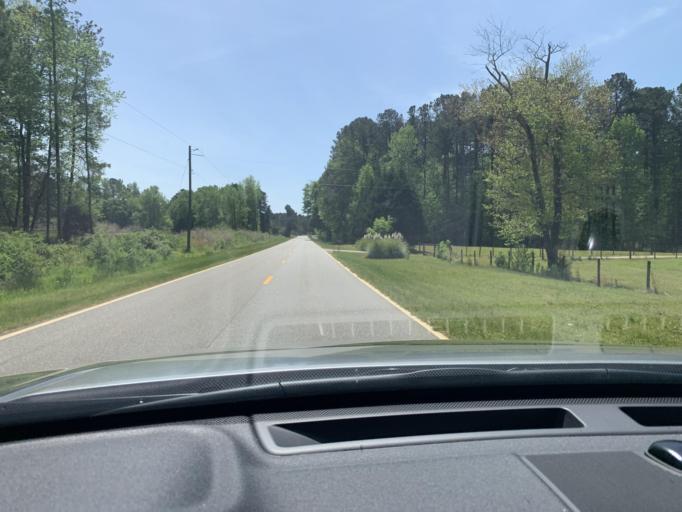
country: US
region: Georgia
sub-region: Oconee County
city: Bogart
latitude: 33.8668
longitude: -83.5683
